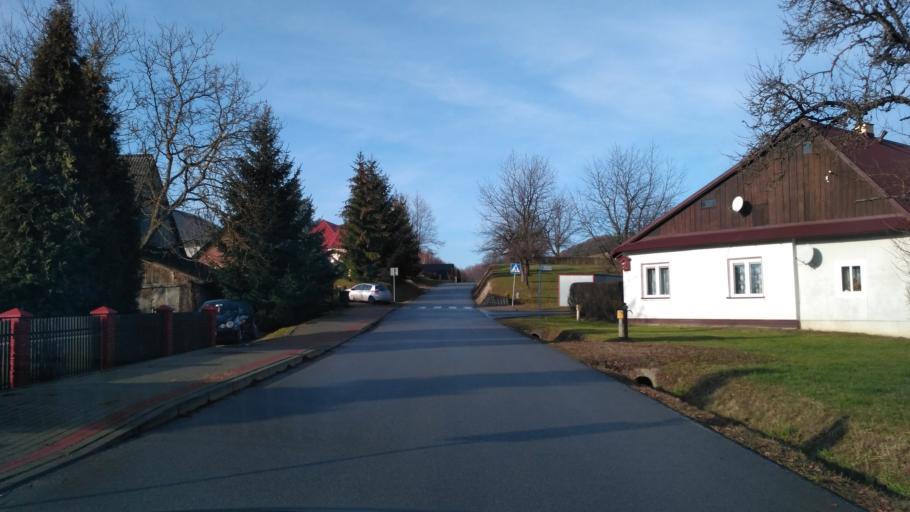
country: PL
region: Subcarpathian Voivodeship
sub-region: Powiat krosnienski
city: Korczyna
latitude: 49.7220
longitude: 21.8070
